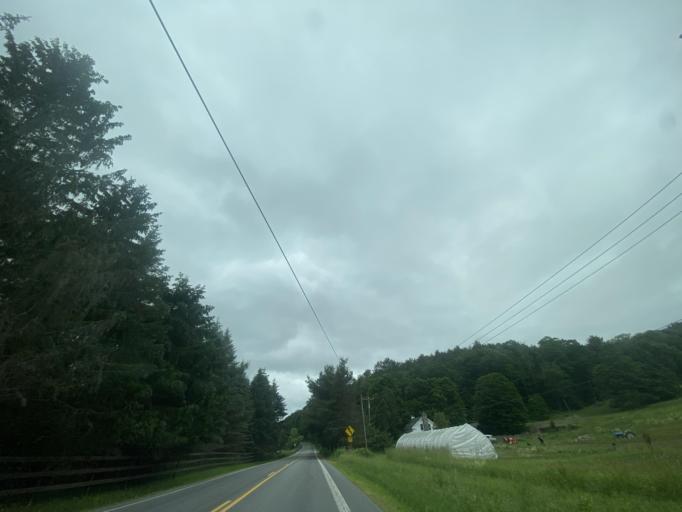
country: US
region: New York
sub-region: Schoharie County
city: Middleburgh
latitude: 42.3827
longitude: -74.3904
